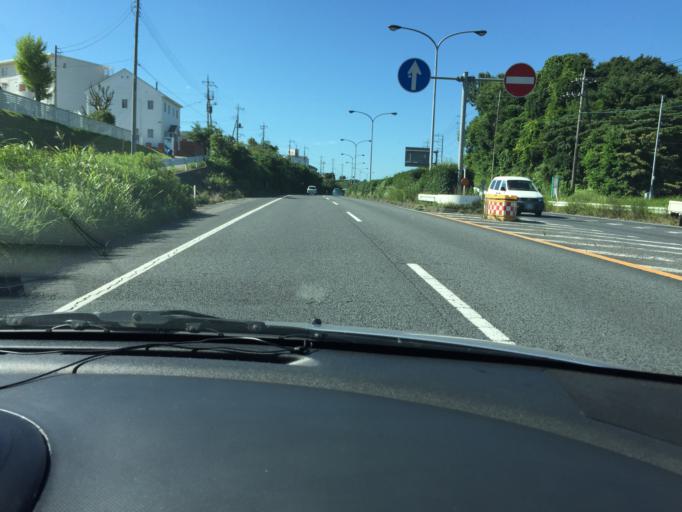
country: JP
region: Ibaraki
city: Naka
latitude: 36.0734
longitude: 140.1791
